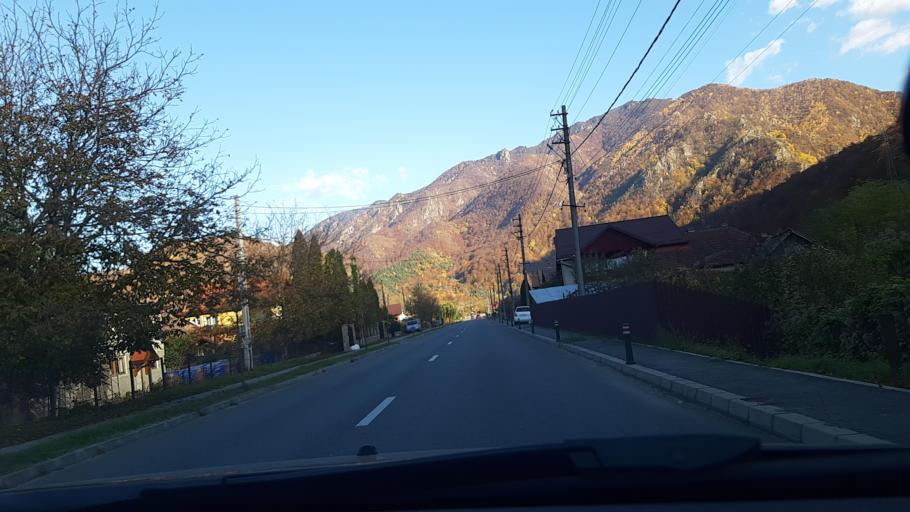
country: RO
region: Valcea
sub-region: Comuna Brezoi
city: Brezoi
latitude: 45.3334
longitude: 24.2637
